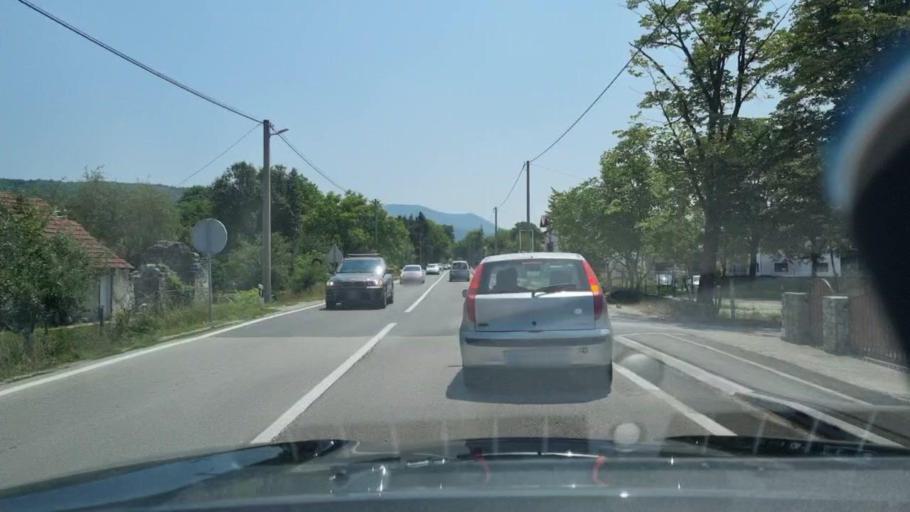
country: BA
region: Federation of Bosnia and Herzegovina
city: Bihac
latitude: 44.7949
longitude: 15.9216
